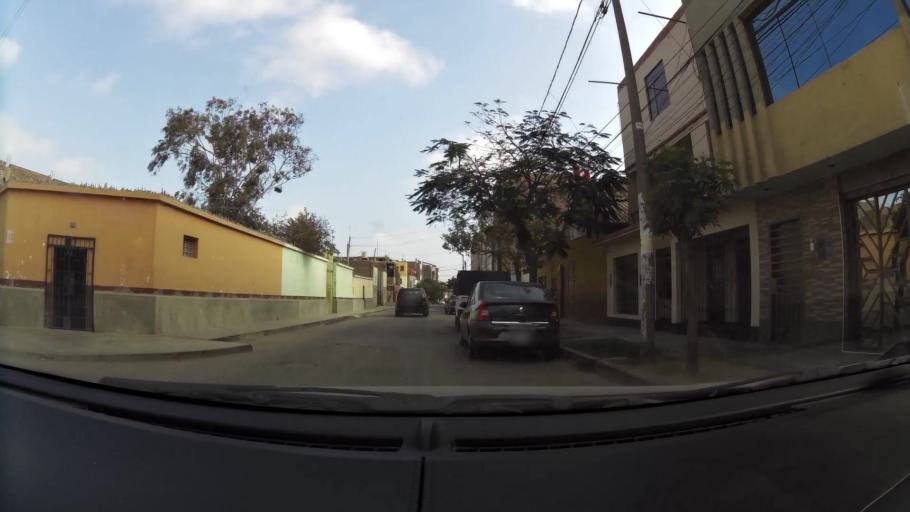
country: PE
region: La Libertad
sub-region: Provincia de Trujillo
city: Trujillo
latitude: -8.1066
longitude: -79.0169
